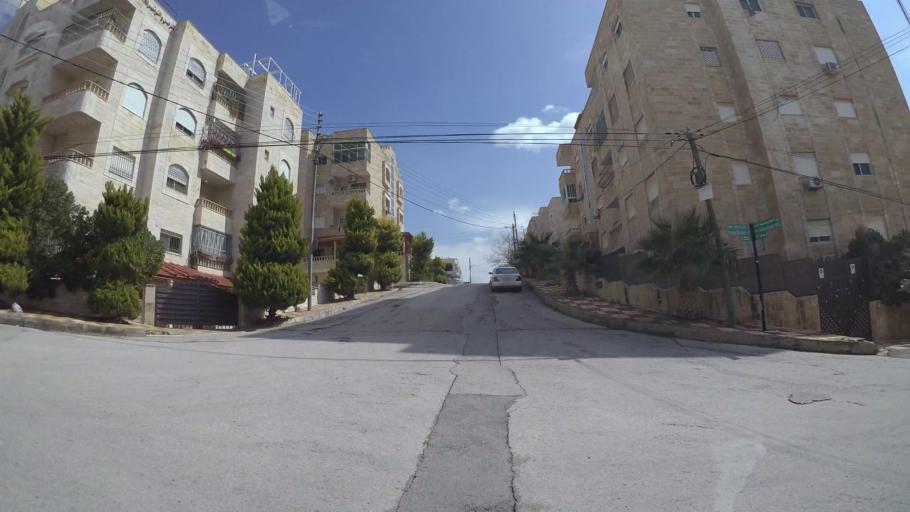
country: JO
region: Amman
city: Al Jubayhah
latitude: 31.9963
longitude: 35.9071
